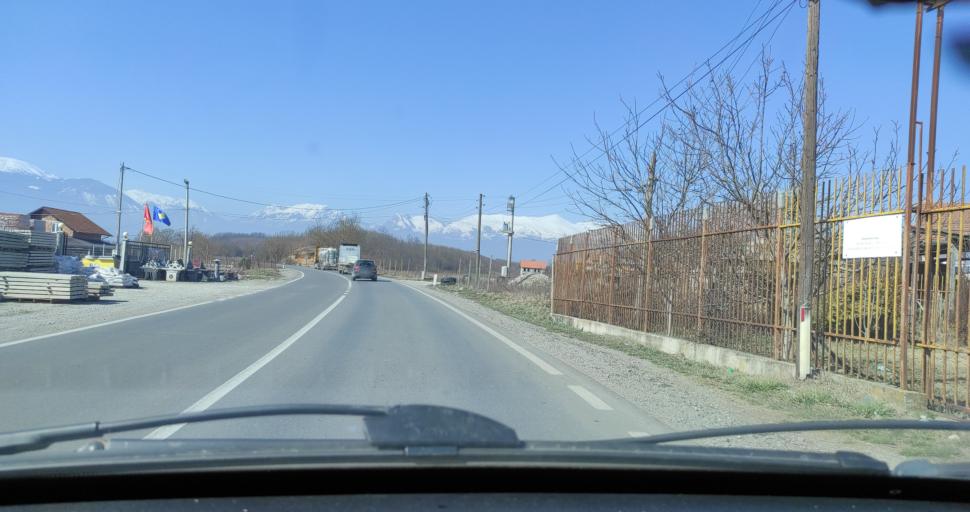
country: XK
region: Pec
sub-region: Komuna e Pejes
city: Kosuriq
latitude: 42.6363
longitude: 20.4451
